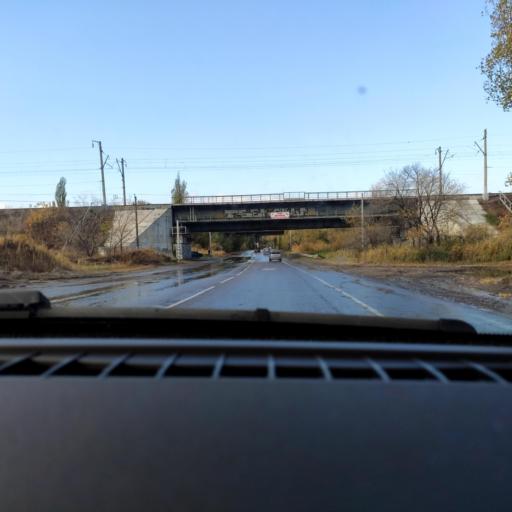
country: RU
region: Voronezj
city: Maslovka
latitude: 51.6224
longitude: 39.2592
